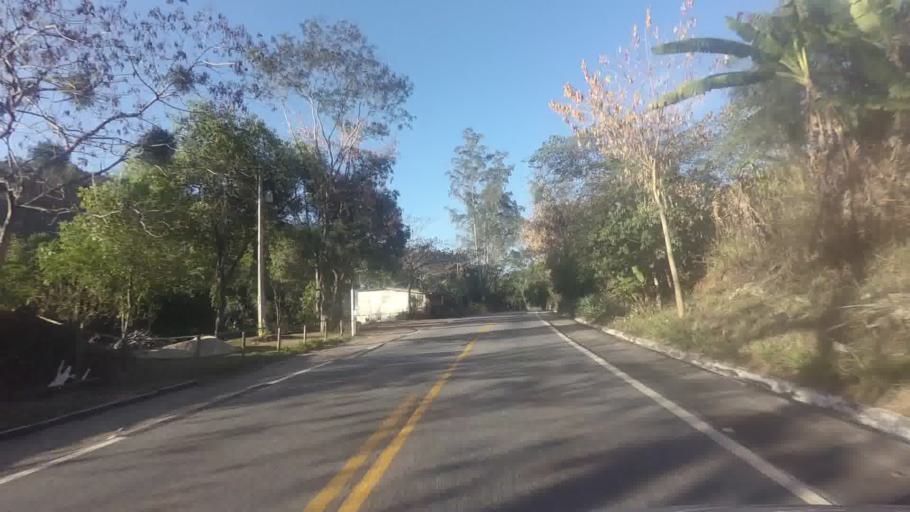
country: BR
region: Espirito Santo
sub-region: Cachoeiro De Itapemirim
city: Cachoeiro de Itapemirim
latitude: -20.8564
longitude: -41.2492
